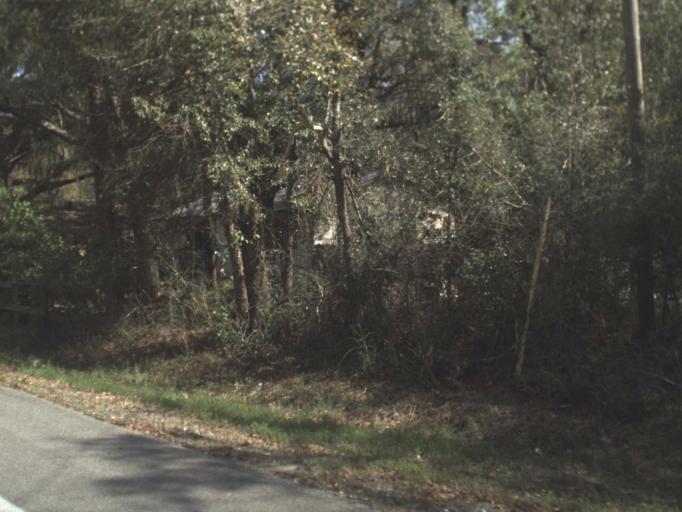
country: US
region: Florida
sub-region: Wakulla County
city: Crawfordville
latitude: 30.0684
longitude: -84.4558
